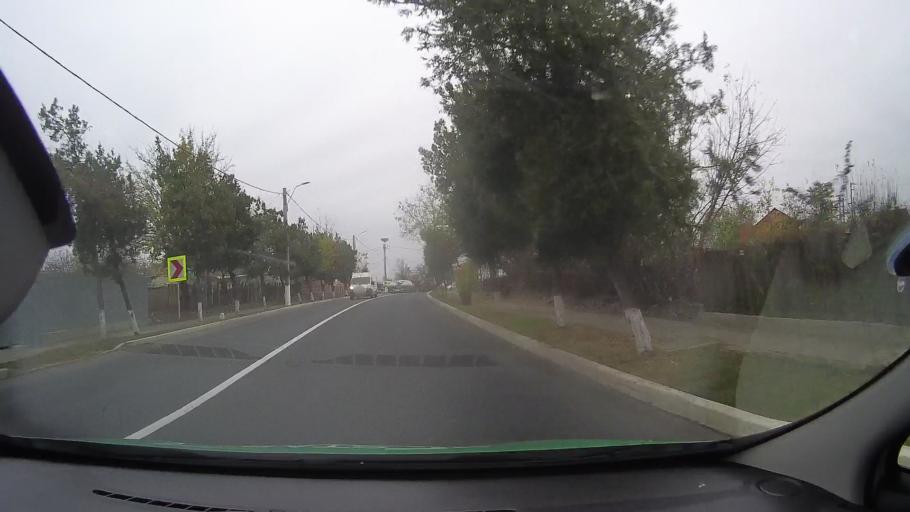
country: RO
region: Constanta
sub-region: Oras Harsova
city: Harsova
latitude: 44.6903
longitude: 27.9415
